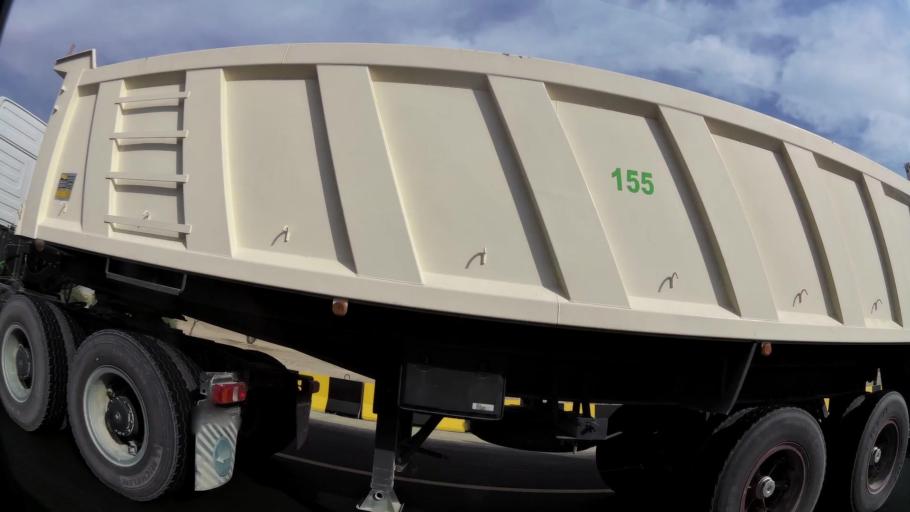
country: KW
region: Muhafazat al Jahra'
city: Al Jahra'
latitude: 29.2859
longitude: 47.7789
